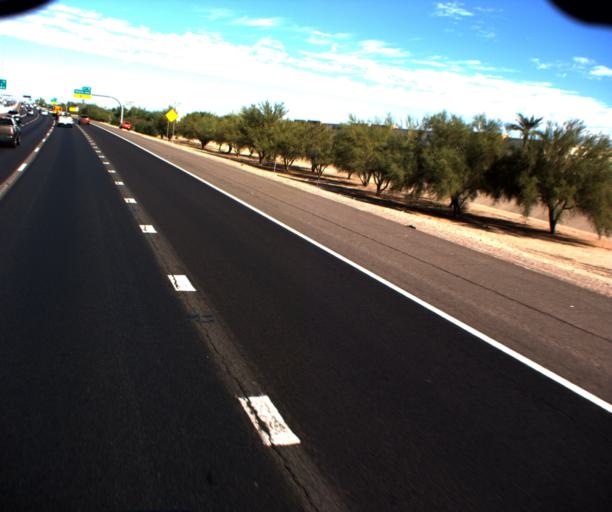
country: US
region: Arizona
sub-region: Maricopa County
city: Peoria
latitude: 33.5718
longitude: -112.2573
